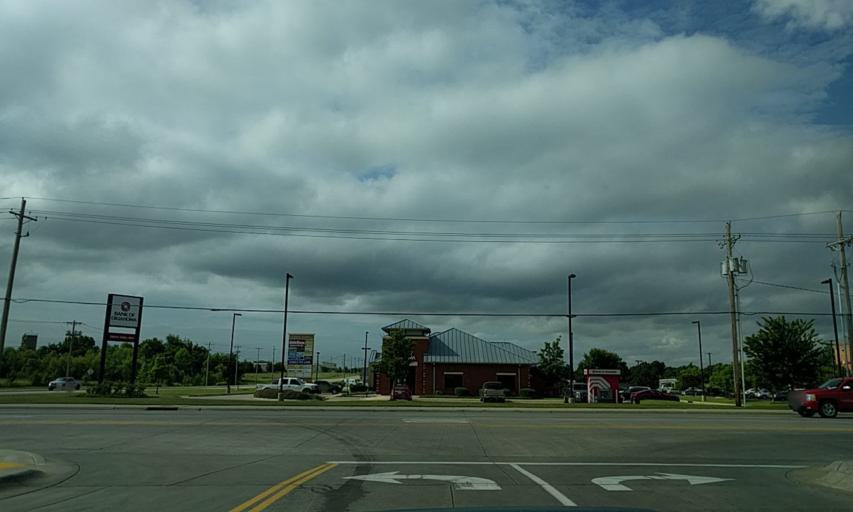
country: US
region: Oklahoma
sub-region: Tulsa County
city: Owasso
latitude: 36.2933
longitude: -95.8488
